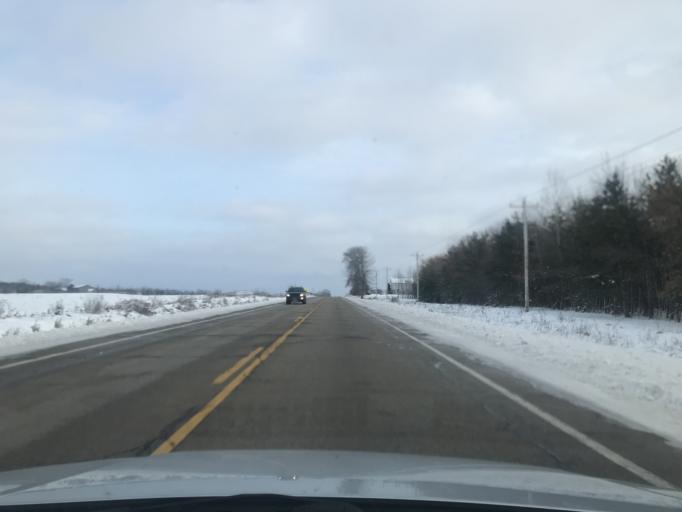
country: US
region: Wisconsin
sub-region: Oconto County
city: Oconto
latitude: 44.8927
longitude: -87.9480
